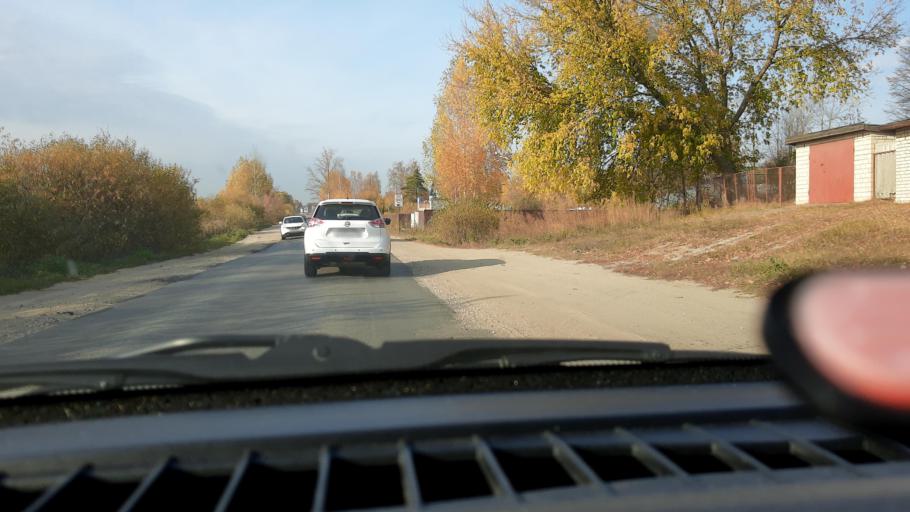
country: RU
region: Nizjnij Novgorod
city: Neklyudovo
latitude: 56.4137
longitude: 43.9734
